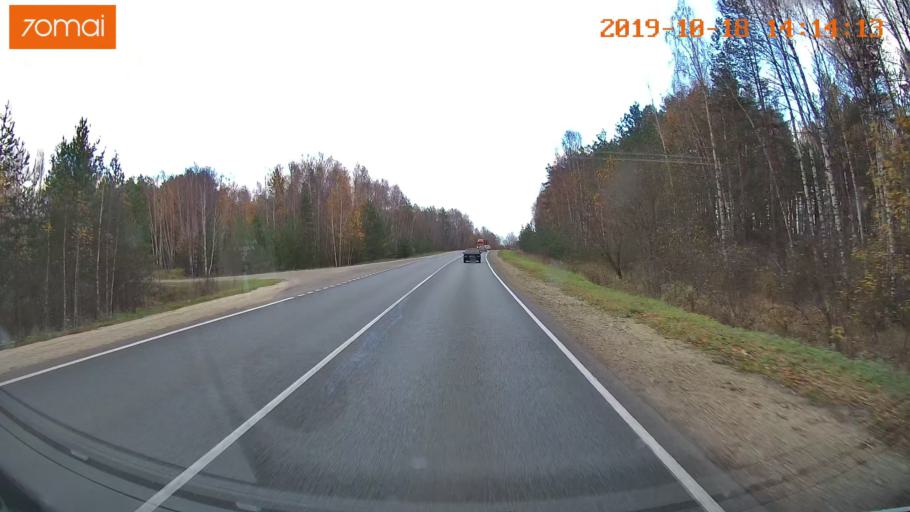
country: RU
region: Rjazan
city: Spas-Klepiki
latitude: 55.1520
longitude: 40.2898
